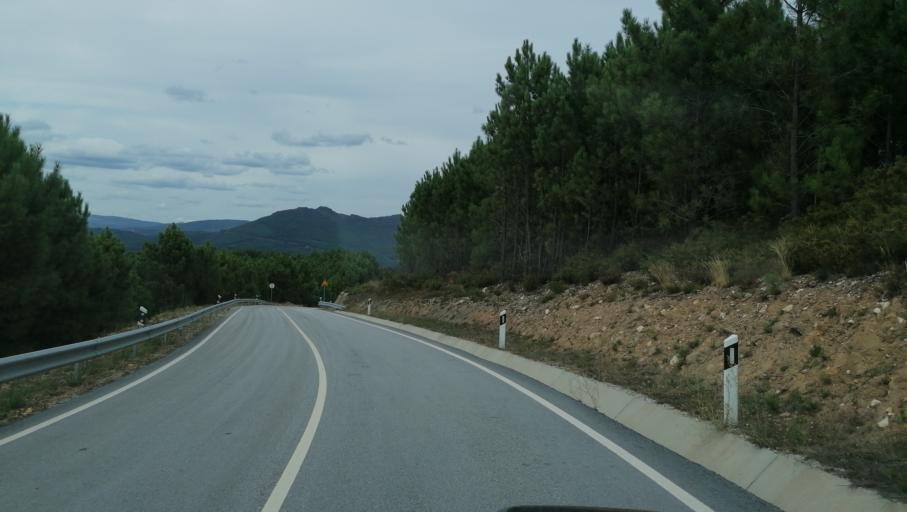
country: PT
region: Vila Real
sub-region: Vila Pouca de Aguiar
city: Vila Pouca de Aguiar
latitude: 41.5622
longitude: -7.7043
